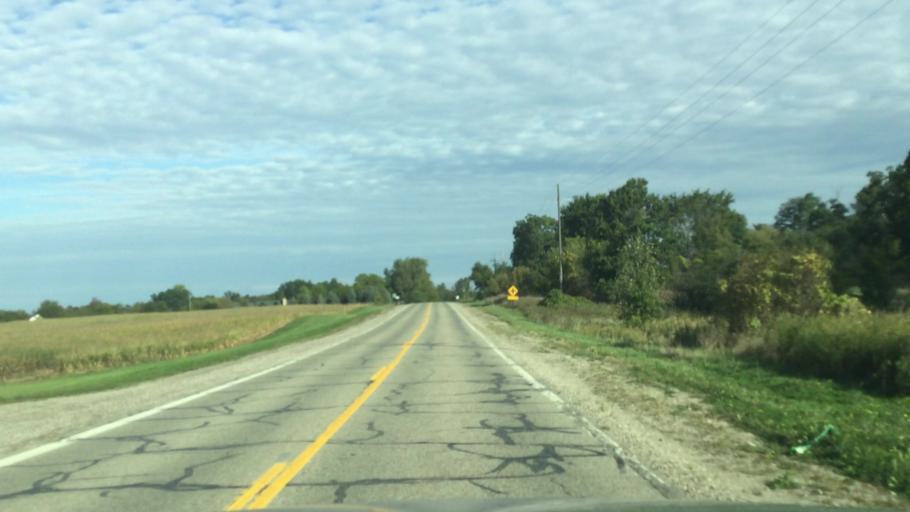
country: US
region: Michigan
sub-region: Livingston County
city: Howell
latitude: 42.5535
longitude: -83.8839
